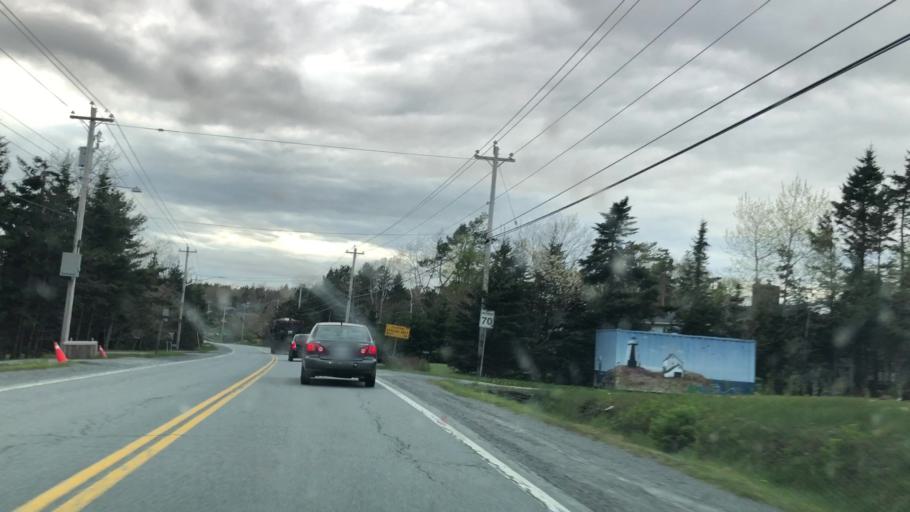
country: CA
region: Nova Scotia
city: Cole Harbour
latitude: 44.7839
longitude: -63.1610
